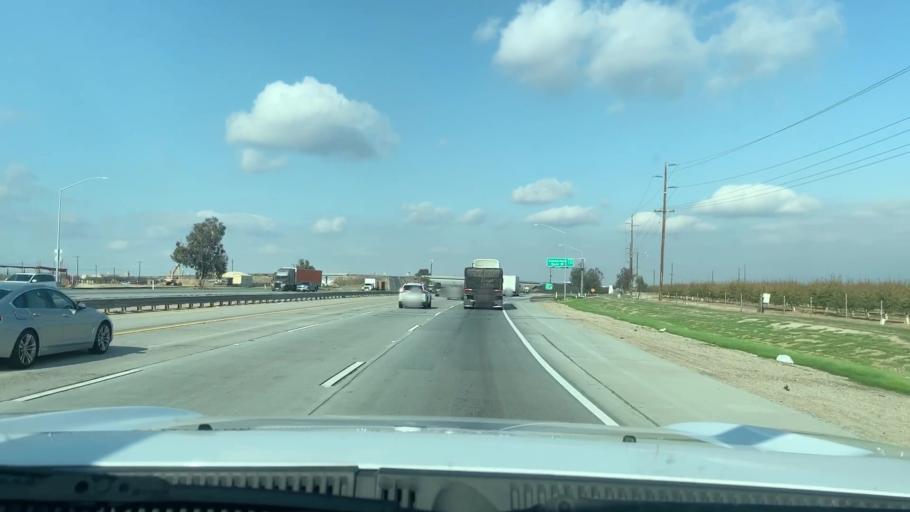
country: US
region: California
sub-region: Kern County
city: Shafter
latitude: 35.5538
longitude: -119.1967
